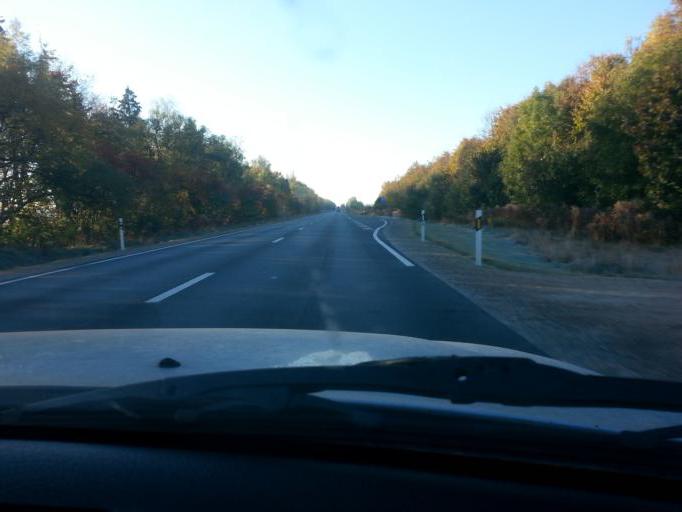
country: LV
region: Jelgava
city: Jelgava
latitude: 56.5202
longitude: 23.7037
